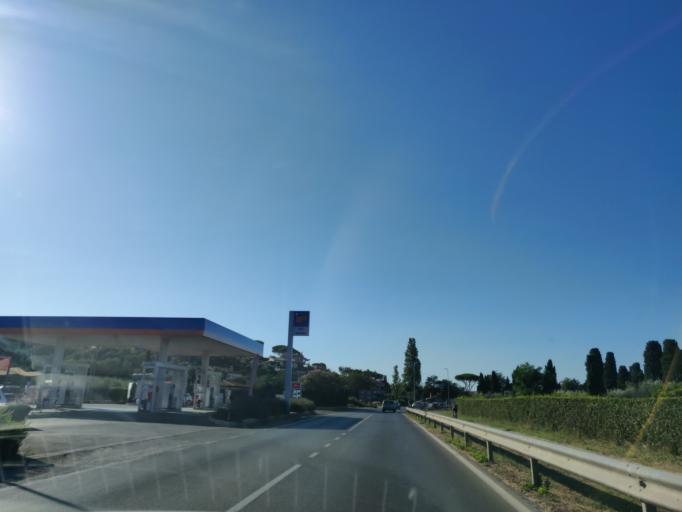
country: IT
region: Tuscany
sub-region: Provincia di Grosseto
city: Porto Ercole
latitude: 42.4254
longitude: 11.1983
